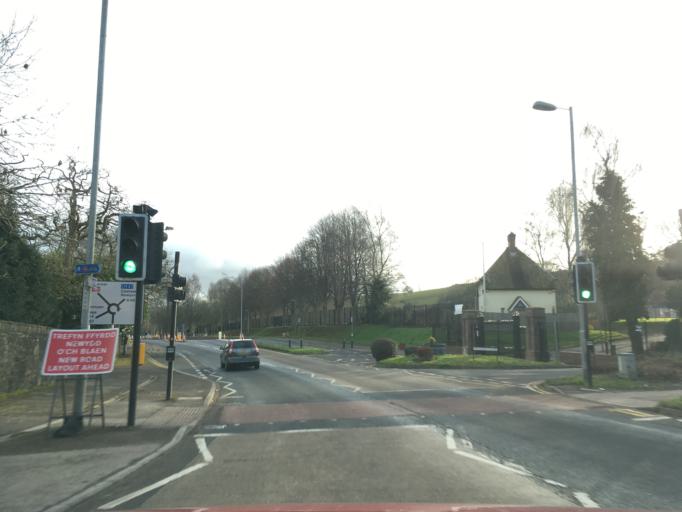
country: GB
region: Wales
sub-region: Newport
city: Newport
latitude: 51.5771
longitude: -3.0448
